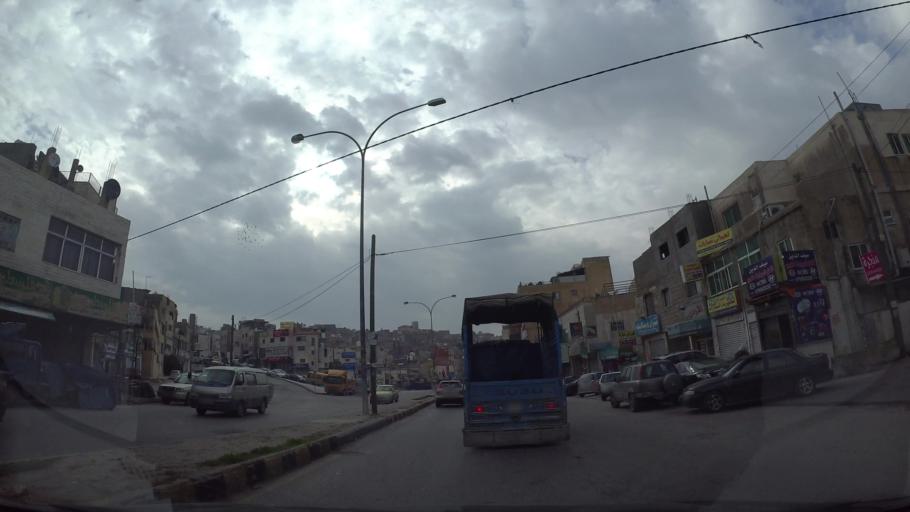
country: JO
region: Amman
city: Amman
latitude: 31.9716
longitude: 35.9252
